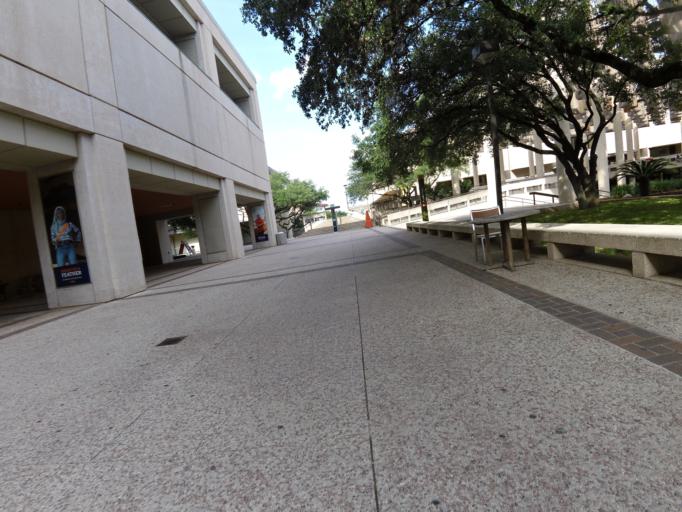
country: US
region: Texas
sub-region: Bexar County
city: Shavano Park
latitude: 29.5843
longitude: -98.6187
